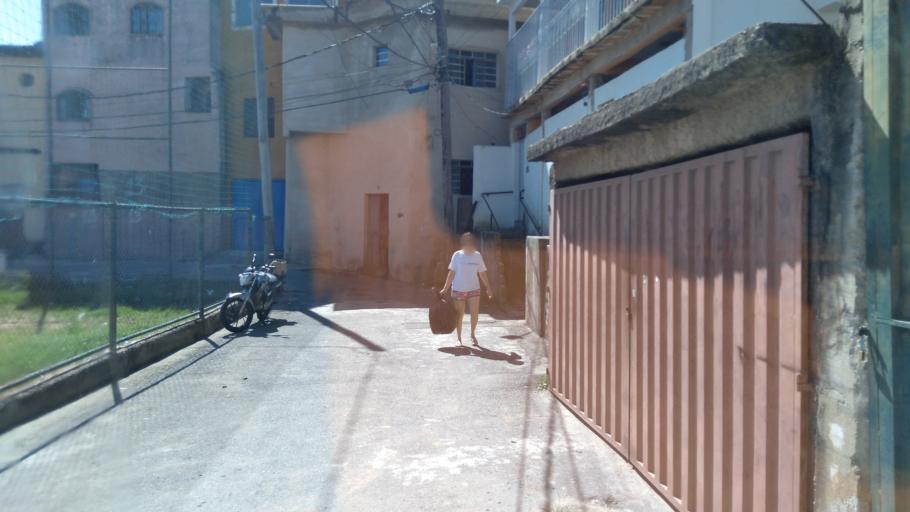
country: BR
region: Minas Gerais
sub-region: Belo Horizonte
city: Belo Horizonte
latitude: -19.8664
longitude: -43.9236
